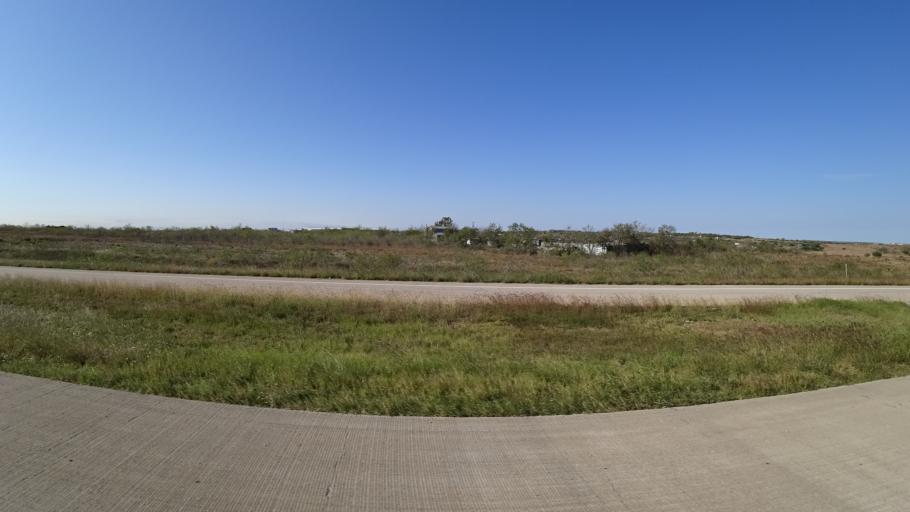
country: US
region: Texas
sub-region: Travis County
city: Garfield
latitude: 30.1244
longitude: -97.6617
